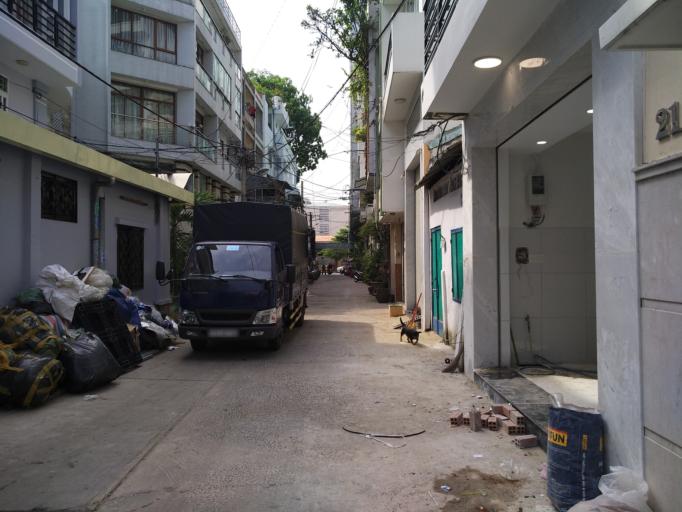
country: VN
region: Ho Chi Minh City
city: Quan Nam
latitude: 10.7591
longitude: 106.6743
